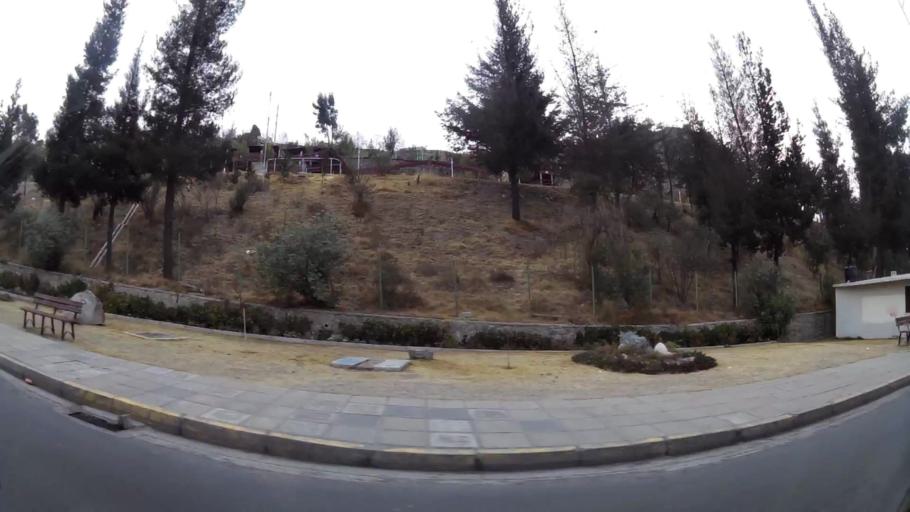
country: BO
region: La Paz
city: La Paz
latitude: -16.5047
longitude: -68.1255
